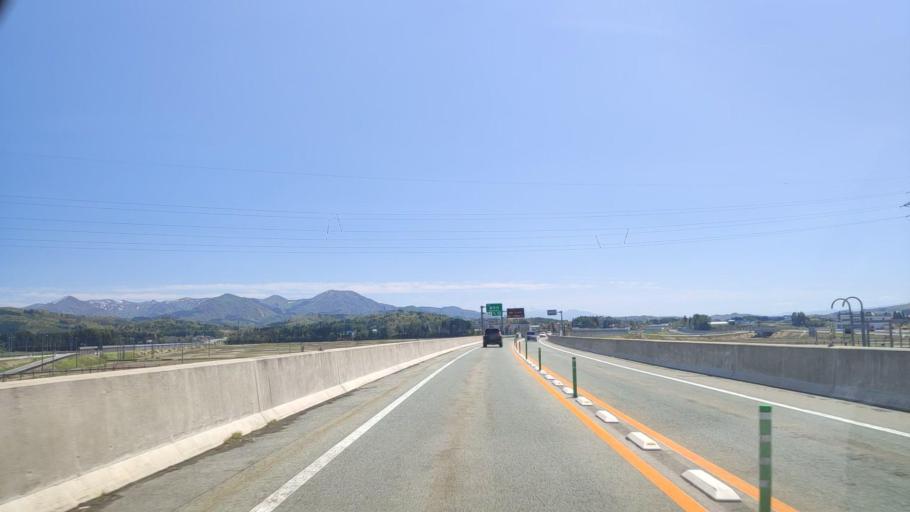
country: JP
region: Yamagata
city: Obanazawa
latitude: 38.6114
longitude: 140.3883
